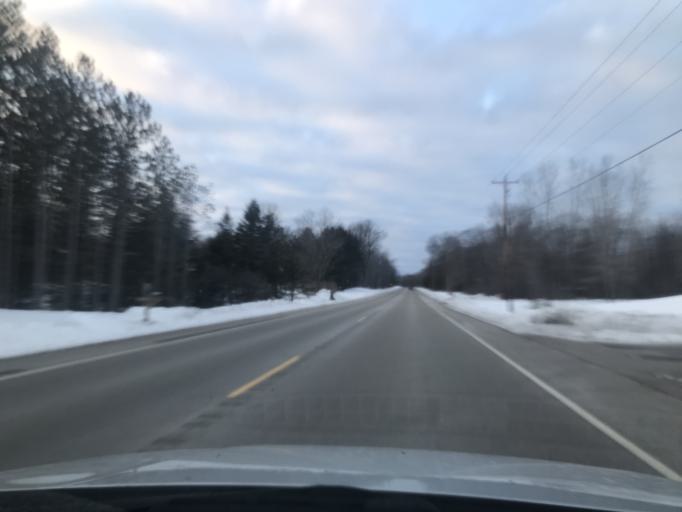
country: US
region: Wisconsin
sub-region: Marinette County
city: Marinette
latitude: 45.1487
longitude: -87.7019
